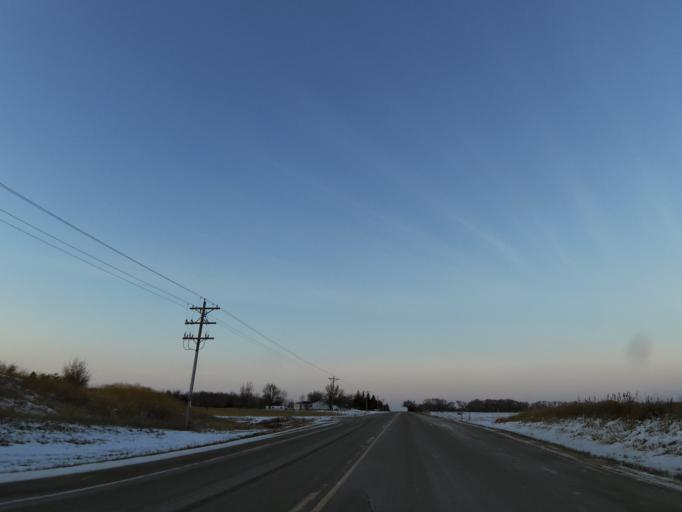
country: US
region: Minnesota
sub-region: Washington County
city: Lake Saint Croix Beach
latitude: 44.9047
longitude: -92.7312
